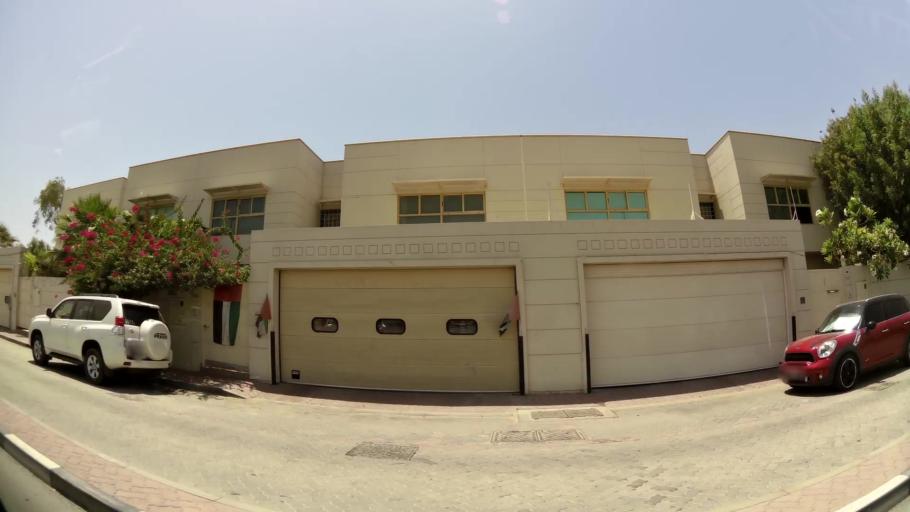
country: AE
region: Dubai
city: Dubai
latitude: 25.2215
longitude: 55.2633
